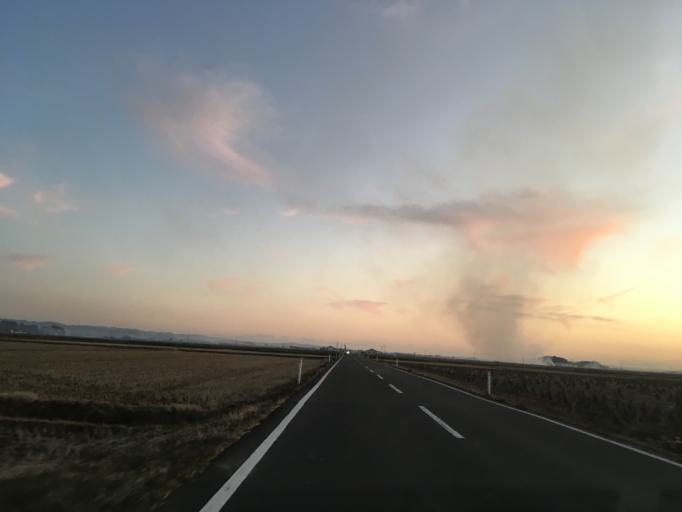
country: JP
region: Iwate
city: Ichinoseki
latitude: 38.7513
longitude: 141.2366
